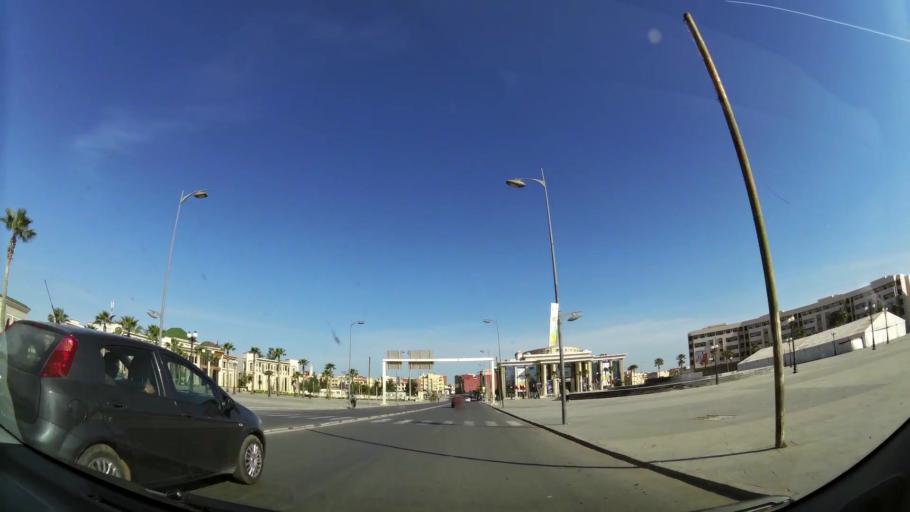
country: MA
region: Oriental
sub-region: Oujda-Angad
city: Oujda
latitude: 34.6771
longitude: -1.9290
